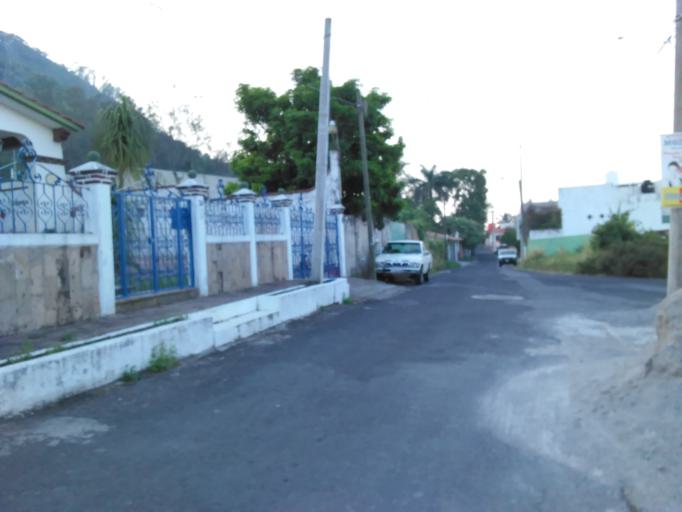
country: MX
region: Nayarit
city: Tepic
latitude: 21.5101
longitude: -104.9220
